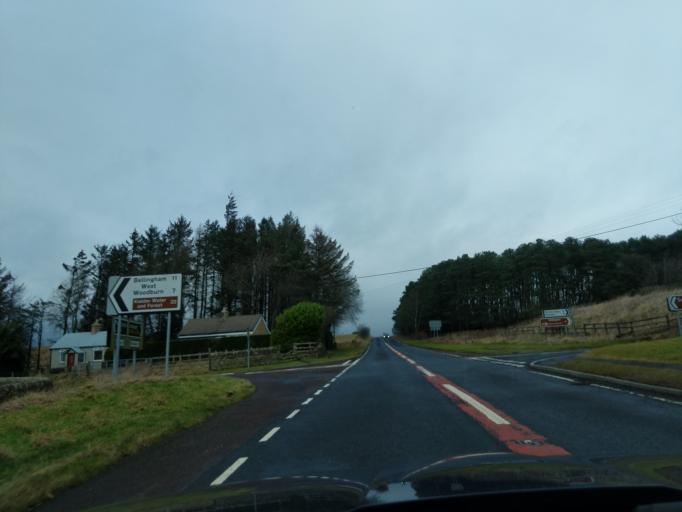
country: GB
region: England
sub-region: Northumberland
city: Rothley
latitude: 55.1656
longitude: -2.0193
